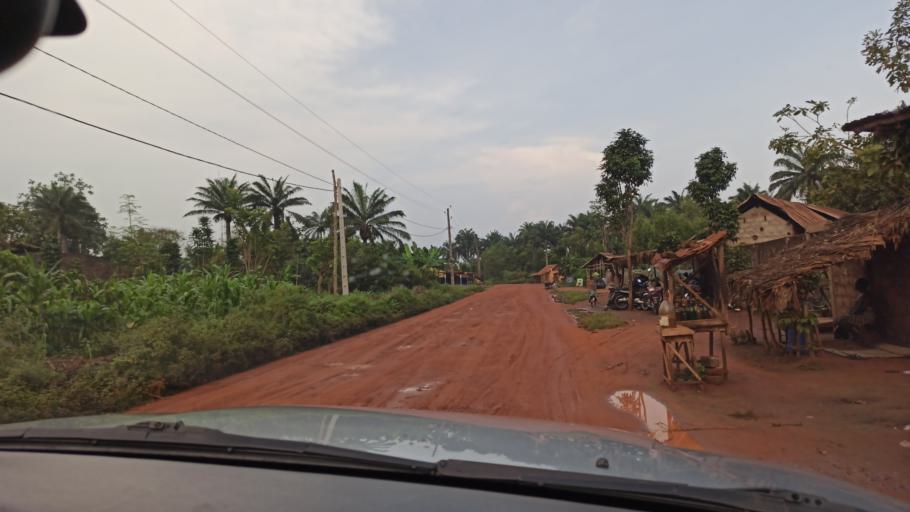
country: BJ
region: Queme
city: Porto-Novo
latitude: 6.4970
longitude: 2.6966
